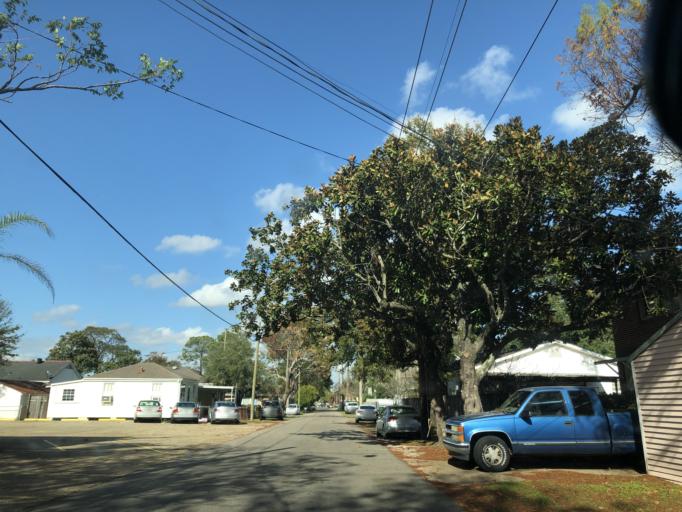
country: US
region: Louisiana
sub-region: Jefferson Parish
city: Metairie Terrace
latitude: 29.9785
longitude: -90.1617
